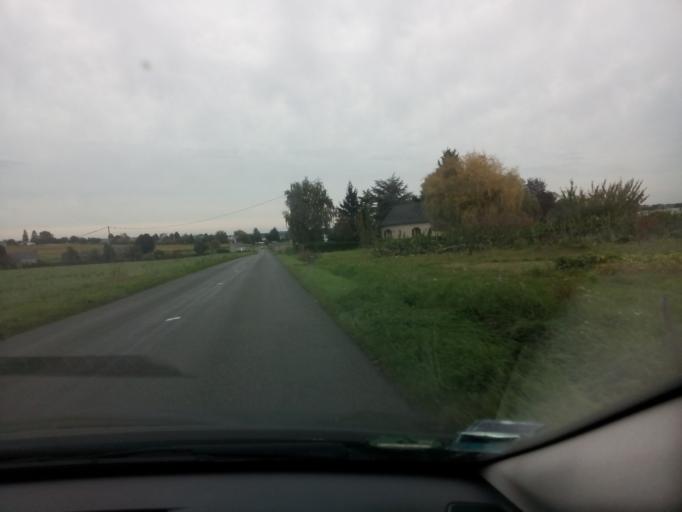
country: FR
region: Pays de la Loire
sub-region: Departement de Maine-et-Loire
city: Baune
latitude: 47.4965
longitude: -0.3310
